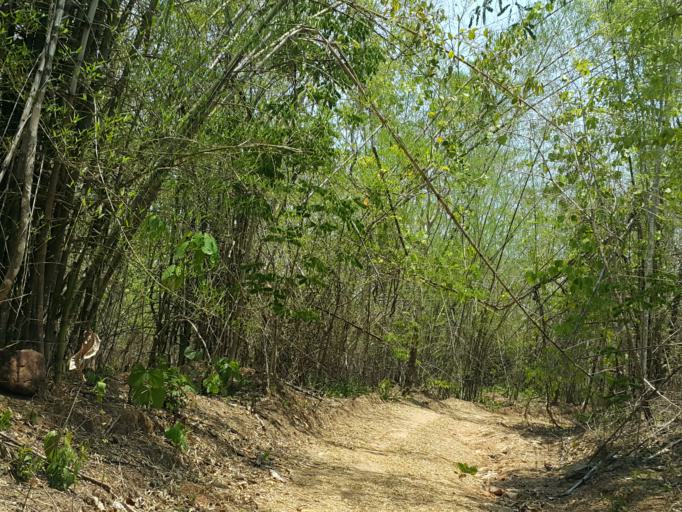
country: TH
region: Kanchanaburi
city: Sai Yok
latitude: 14.2272
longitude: 98.8823
